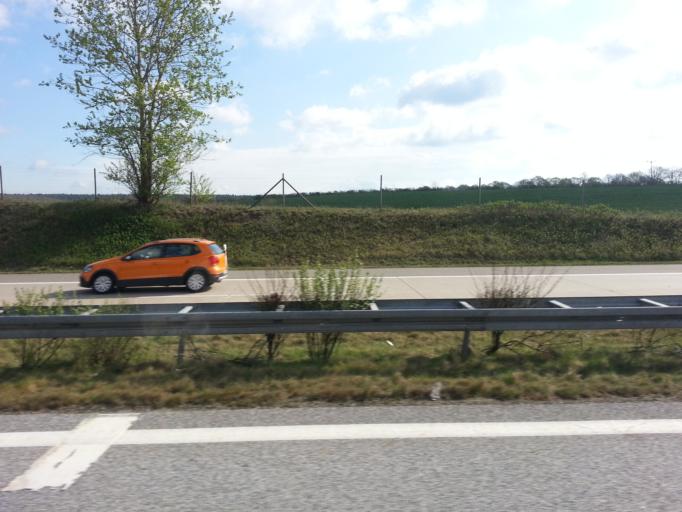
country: DE
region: Mecklenburg-Vorpommern
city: Krakow am See
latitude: 53.6376
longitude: 12.3724
